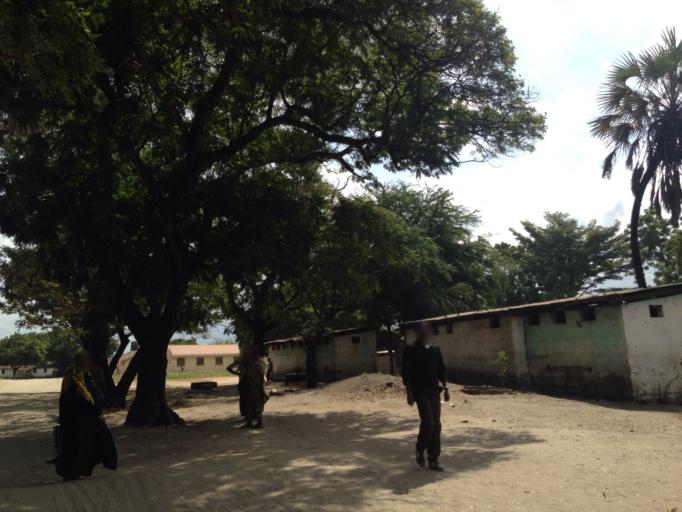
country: TZ
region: Dar es Salaam
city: Dar es Salaam
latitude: -6.8431
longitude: 39.2833
